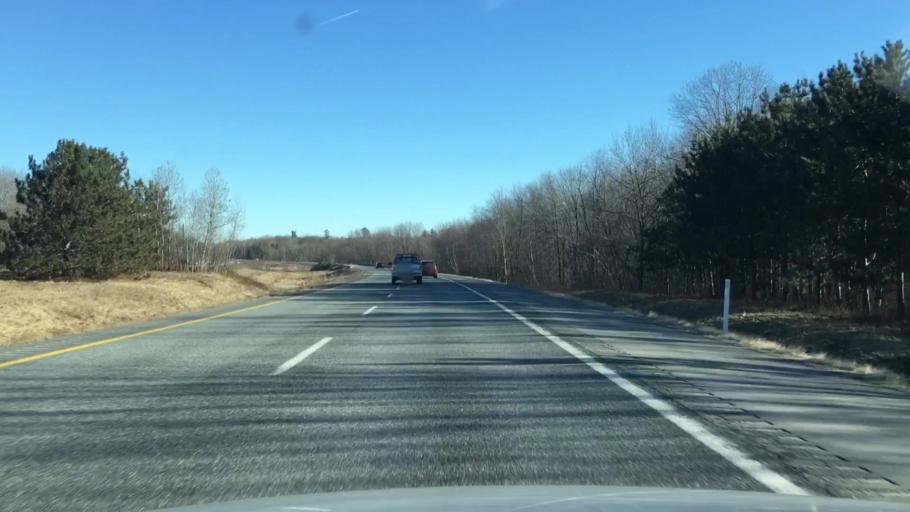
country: US
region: Maine
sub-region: Penobscot County
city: Hermon
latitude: 44.7626
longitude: -68.9137
